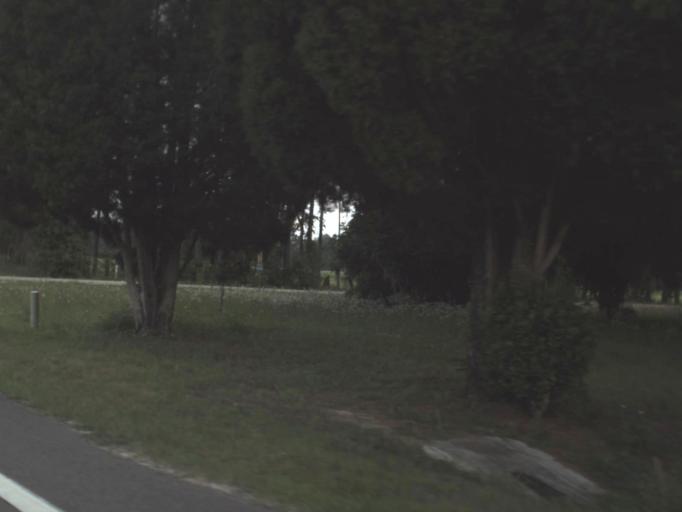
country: US
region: Florida
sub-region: Columbia County
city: Five Points
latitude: 30.3582
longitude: -82.6177
